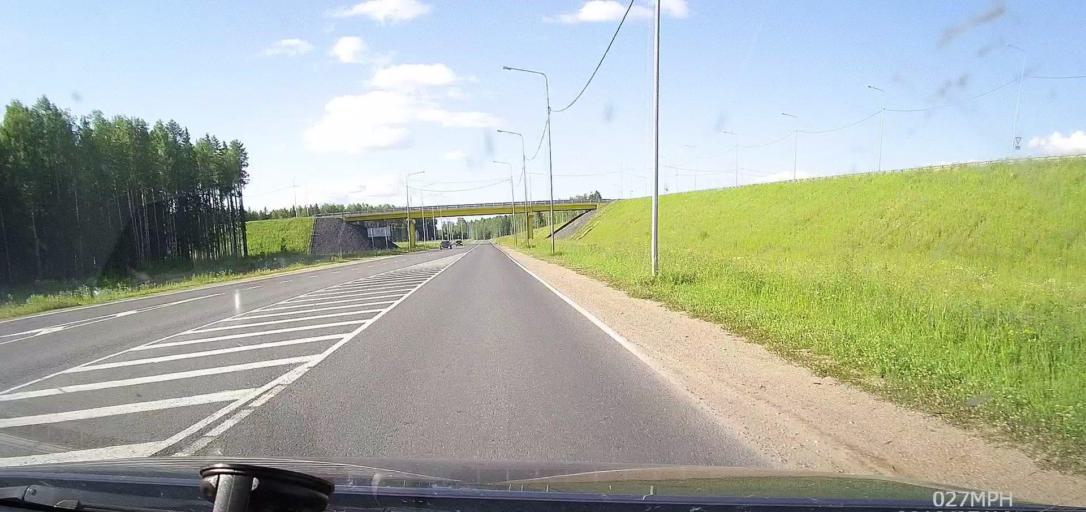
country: RU
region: Arkhangelskaya
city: Mirnyy
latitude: 62.7656
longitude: 40.2994
